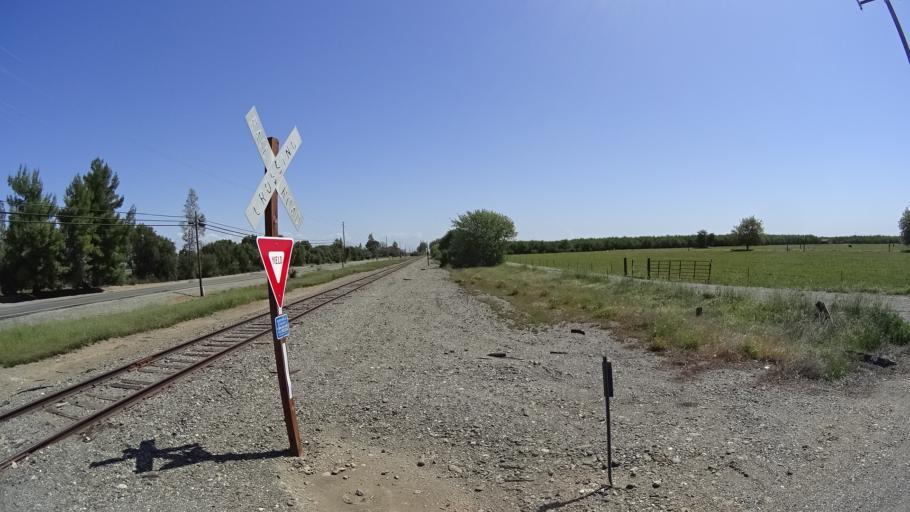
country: US
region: California
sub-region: Glenn County
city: Orland
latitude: 39.7687
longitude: -122.1871
